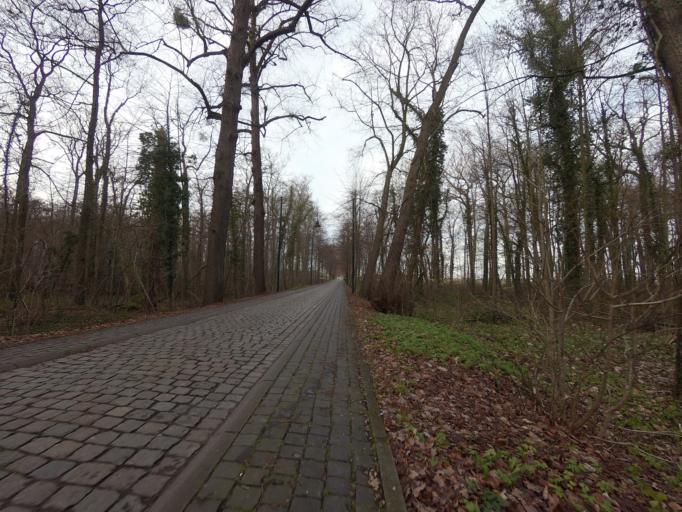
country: BE
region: Flanders
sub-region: Provincie Vlaams-Brabant
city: Kortenberg
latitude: 50.8851
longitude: 4.5623
